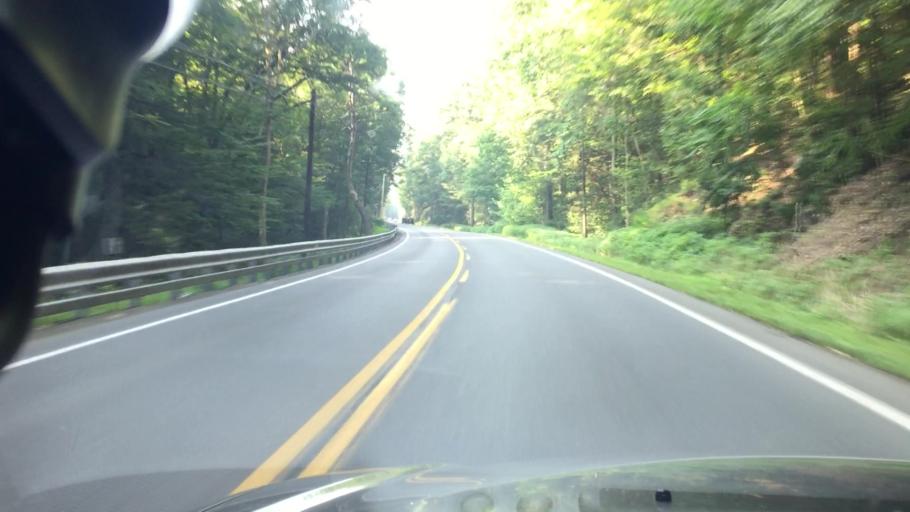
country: US
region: Pennsylvania
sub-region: Northumberland County
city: Elysburg
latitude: 40.8918
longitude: -76.5087
